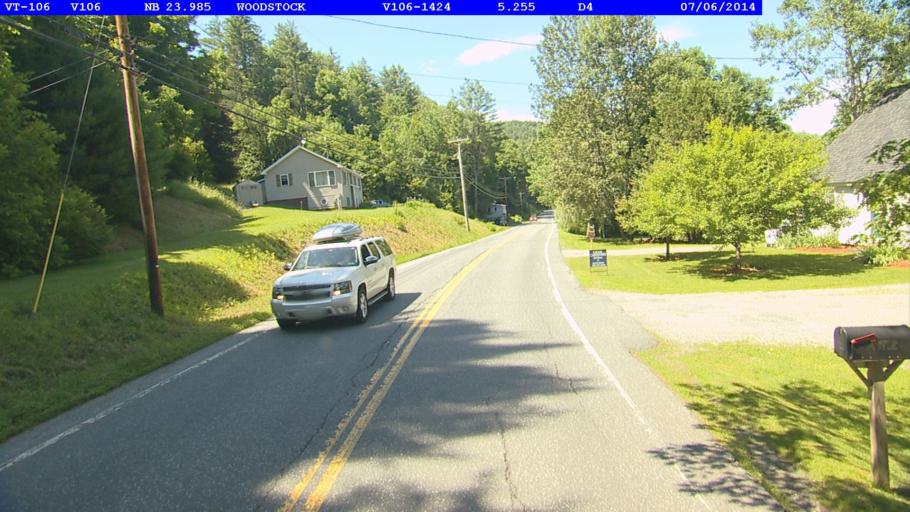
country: US
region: Vermont
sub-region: Windsor County
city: Woodstock
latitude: 43.5962
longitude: -72.5182
